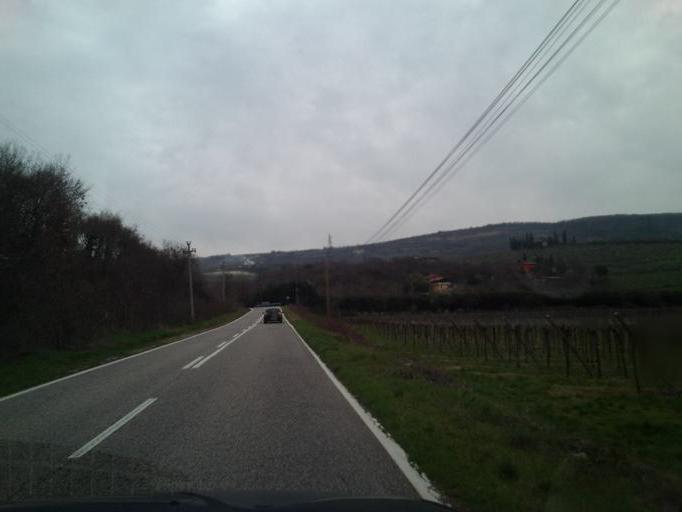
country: IT
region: Veneto
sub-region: Provincia di Verona
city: Montorio
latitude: 45.4784
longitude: 11.0649
